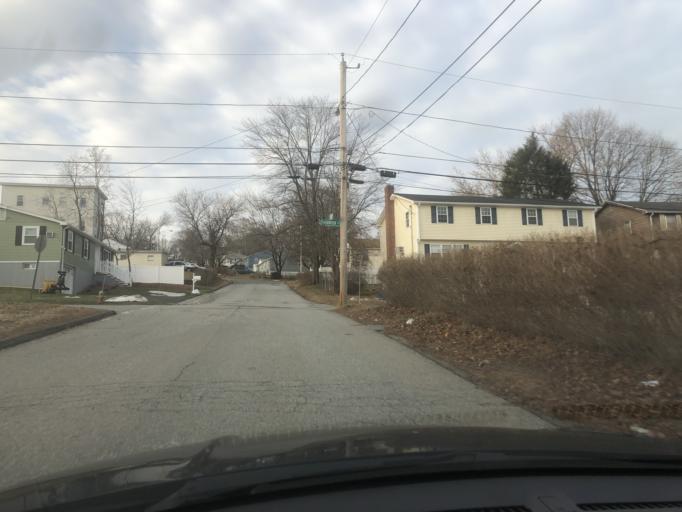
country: US
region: Massachusetts
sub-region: Essex County
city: Lawrence
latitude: 42.7204
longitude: -71.1465
